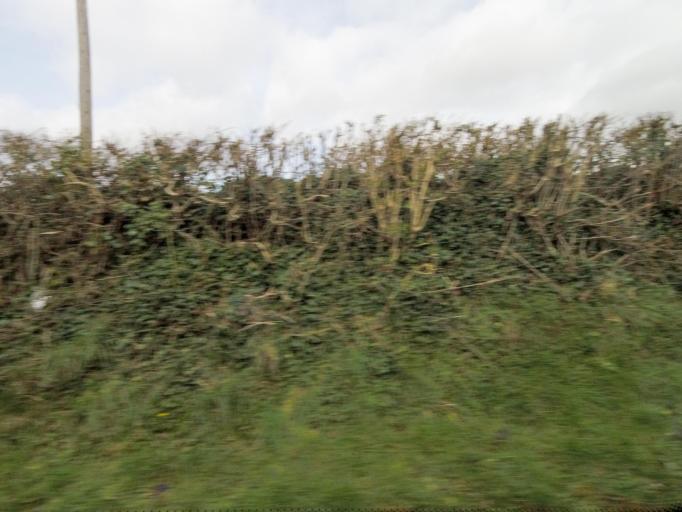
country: IE
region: Leinster
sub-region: Kildare
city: Naas
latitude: 53.1938
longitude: -6.6502
